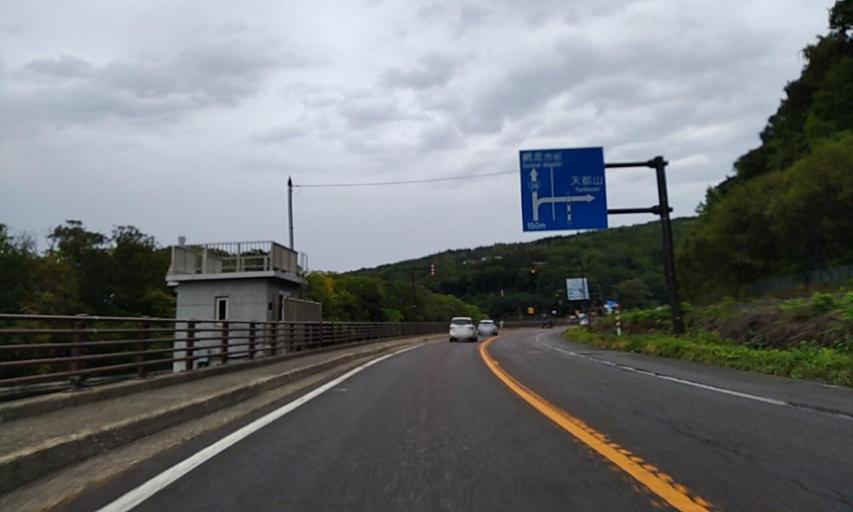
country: JP
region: Hokkaido
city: Abashiri
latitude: 44.0030
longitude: 144.2266
